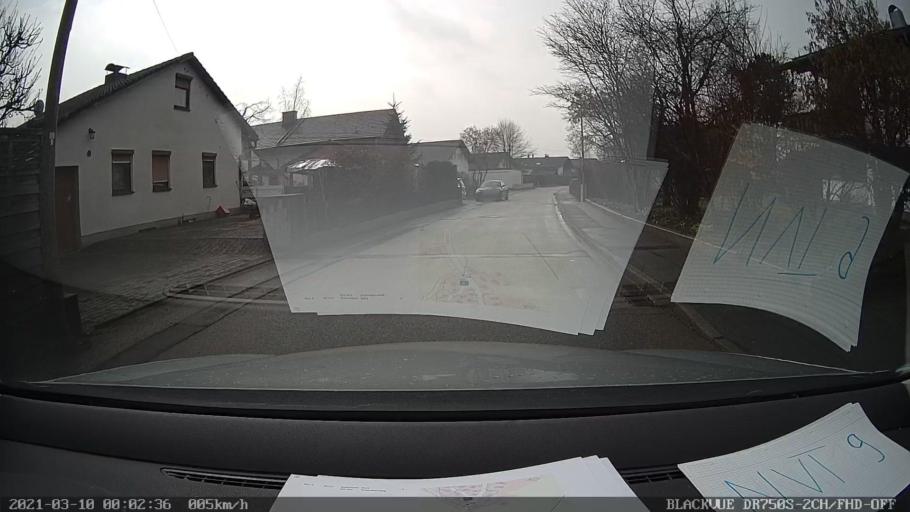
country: DE
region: Bavaria
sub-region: Upper Bavaria
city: Schonstett
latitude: 47.9819
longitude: 12.2465
